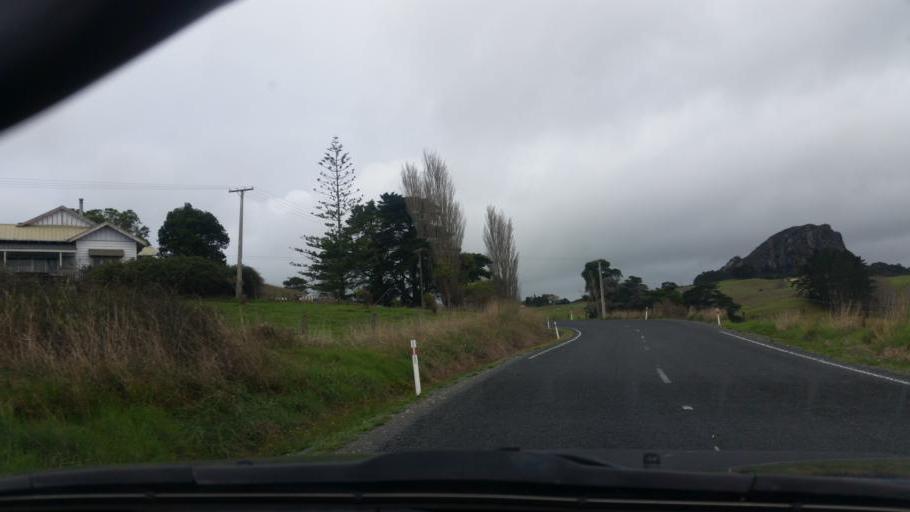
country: NZ
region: Northland
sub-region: Kaipara District
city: Dargaville
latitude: -36.0094
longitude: 173.9745
